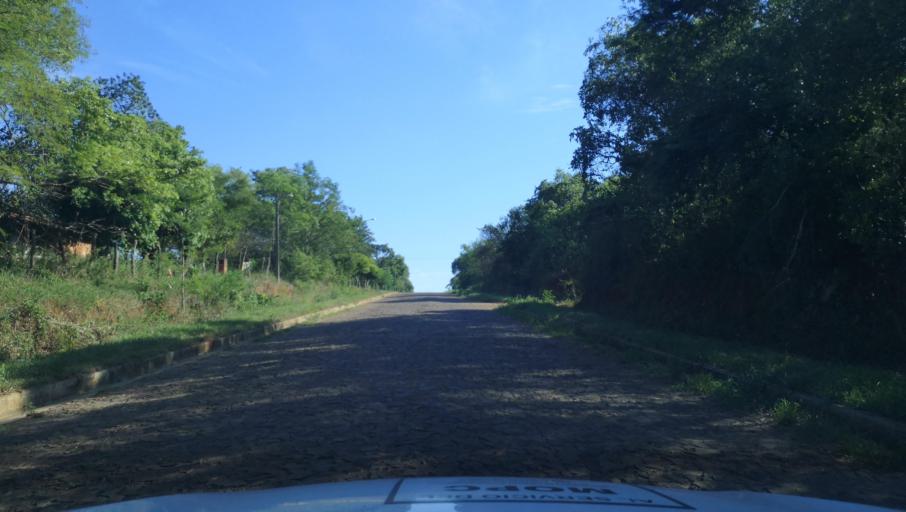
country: PY
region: Misiones
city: Santa Maria
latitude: -26.8796
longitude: -57.0131
